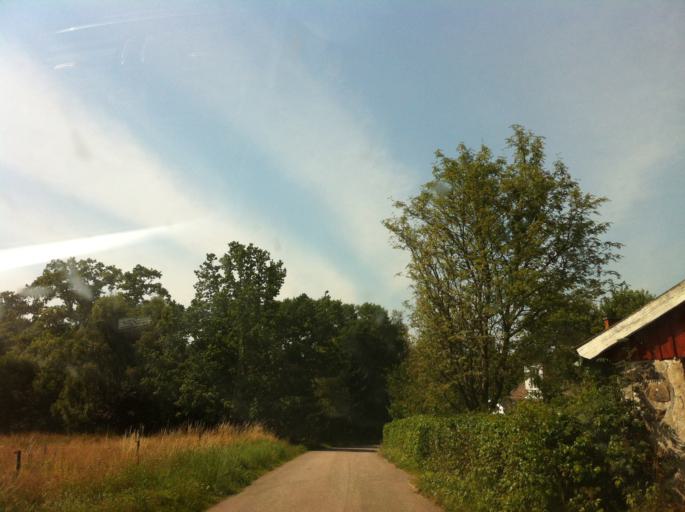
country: SE
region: Skane
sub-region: Eslovs Kommun
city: Stehag
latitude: 55.9816
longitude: 13.4323
